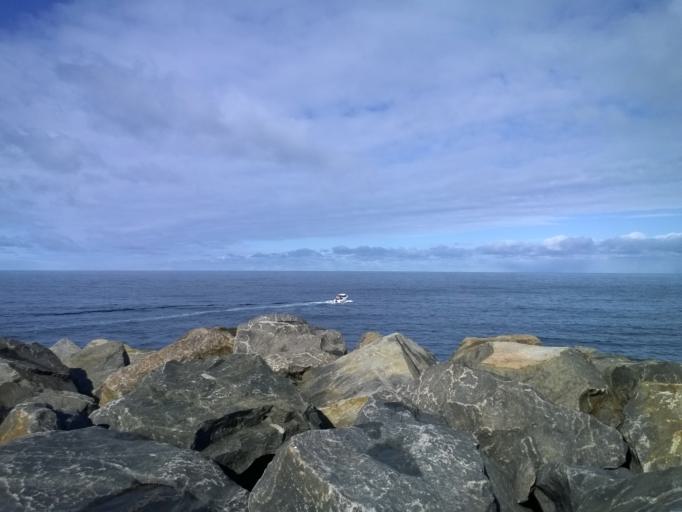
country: NO
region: Nordland
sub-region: Vagan
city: Kabelvag
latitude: 68.3890
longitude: 14.4033
